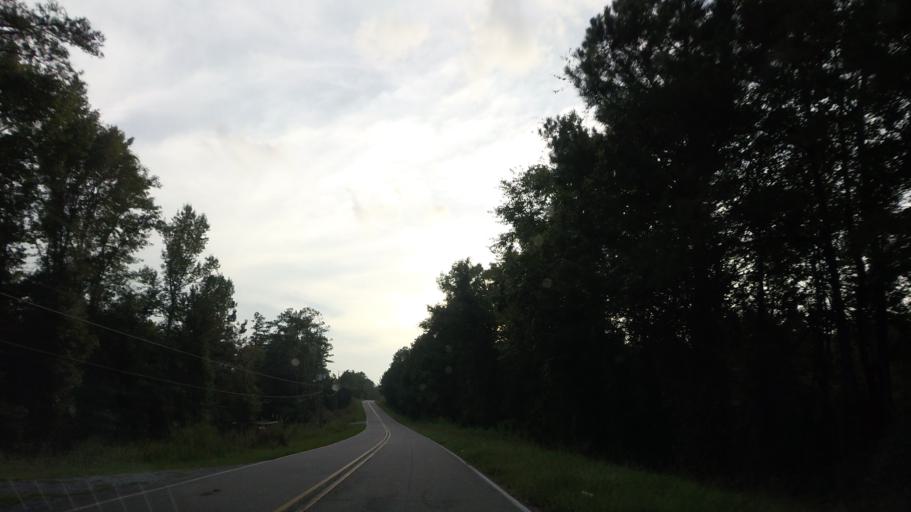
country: US
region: Georgia
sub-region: Bibb County
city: Macon
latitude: 32.8768
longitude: -83.5307
